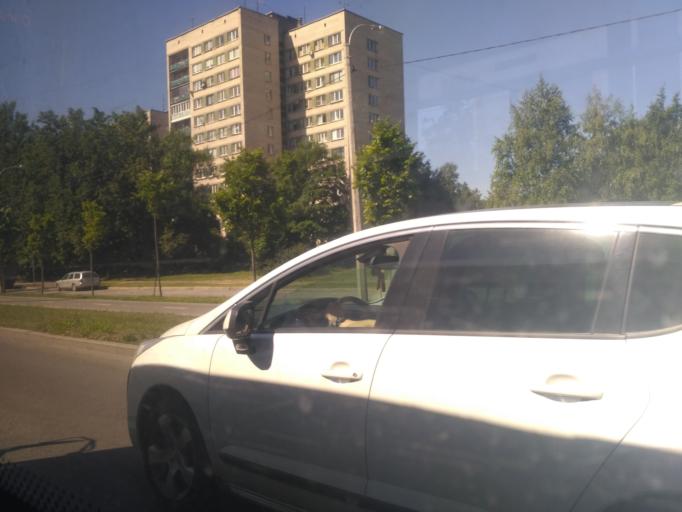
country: RU
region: Leningrad
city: Kalininskiy
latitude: 59.9725
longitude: 30.4129
